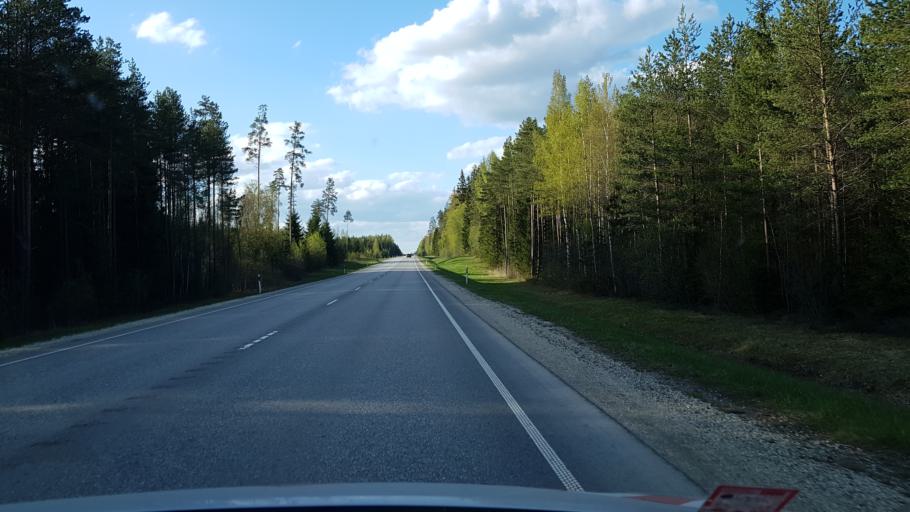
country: EE
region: Vorumaa
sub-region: Voru linn
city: Voru
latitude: 57.9450
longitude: 26.7957
